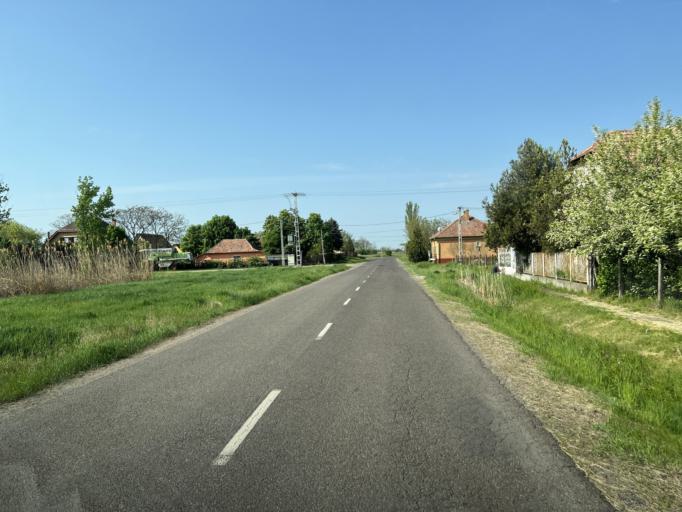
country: HU
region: Pest
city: Jaszkarajeno
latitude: 47.0468
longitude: 20.0722
